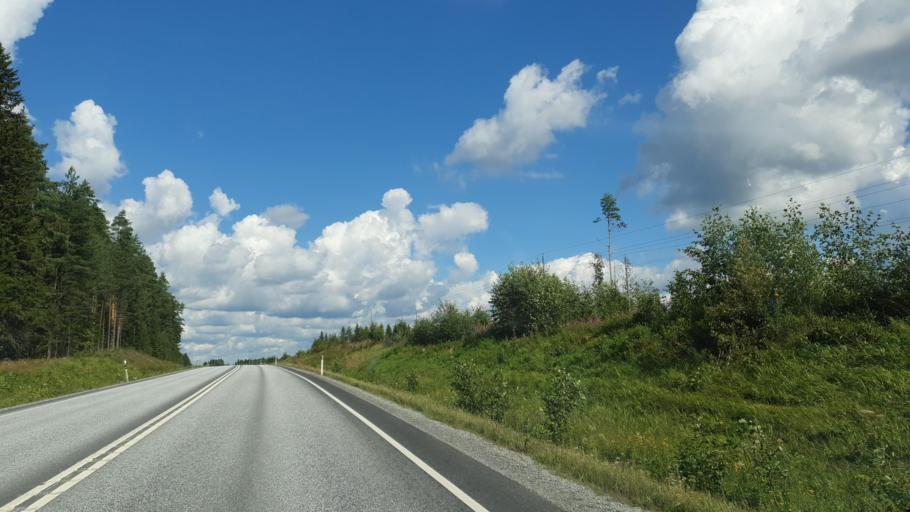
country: FI
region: Northern Savo
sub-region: Ylae-Savo
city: Sonkajaervi
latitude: 63.8499
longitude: 27.4402
